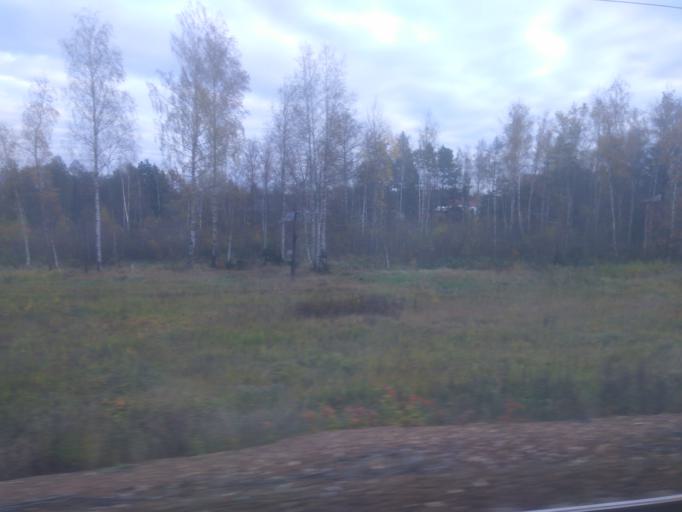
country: RU
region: Moskovskaya
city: Aprelevka
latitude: 55.5689
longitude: 37.0949
